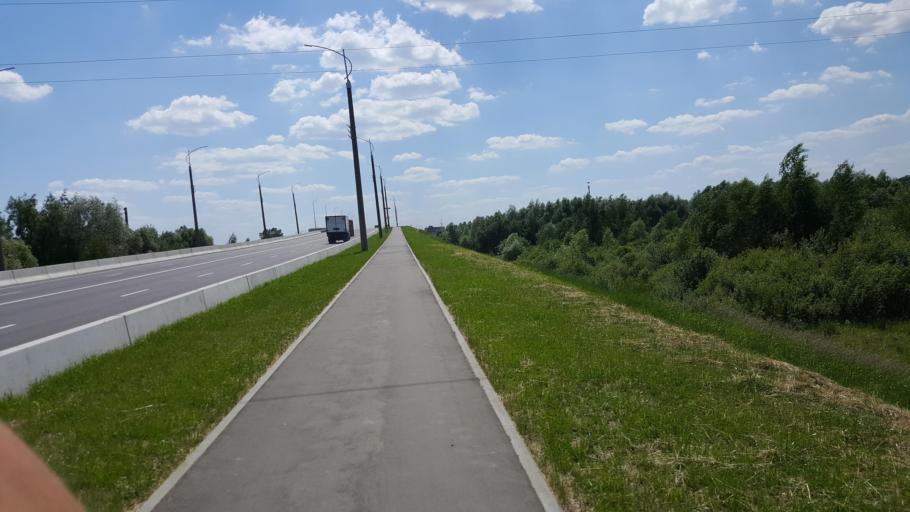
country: BY
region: Brest
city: Kobryn
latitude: 52.2178
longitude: 24.3313
